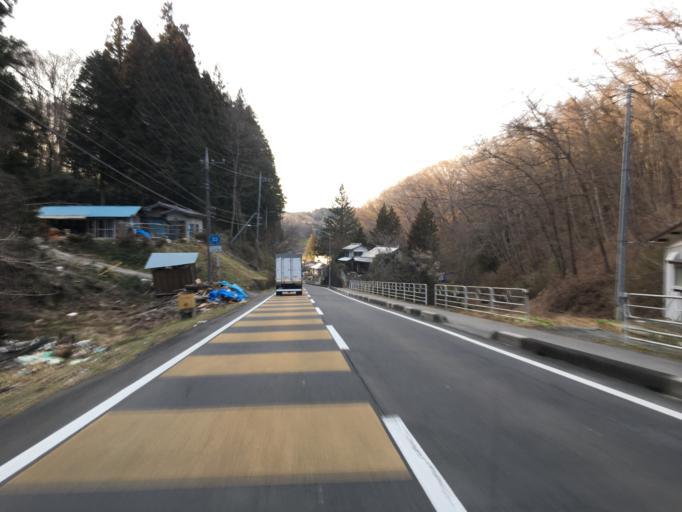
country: JP
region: Ibaraki
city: Daigo
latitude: 36.7845
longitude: 140.4240
